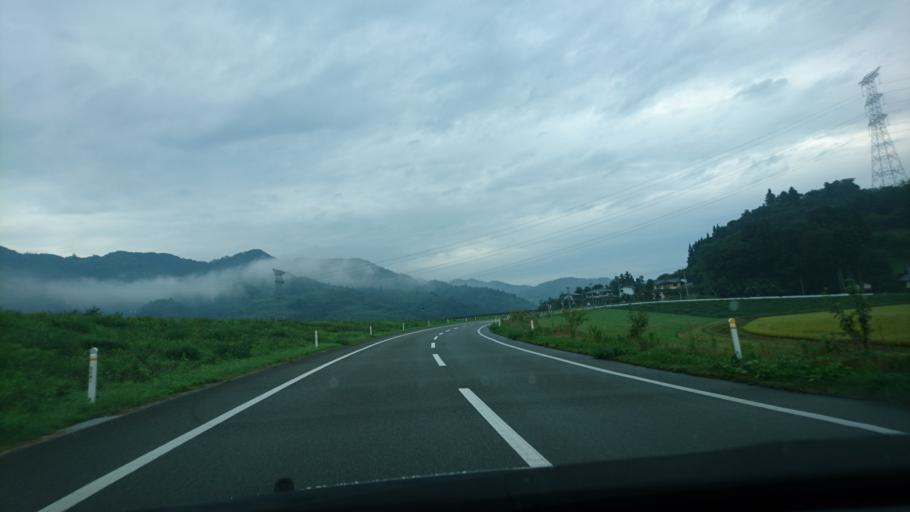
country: JP
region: Iwate
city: Ichinoseki
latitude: 38.9327
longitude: 141.2505
